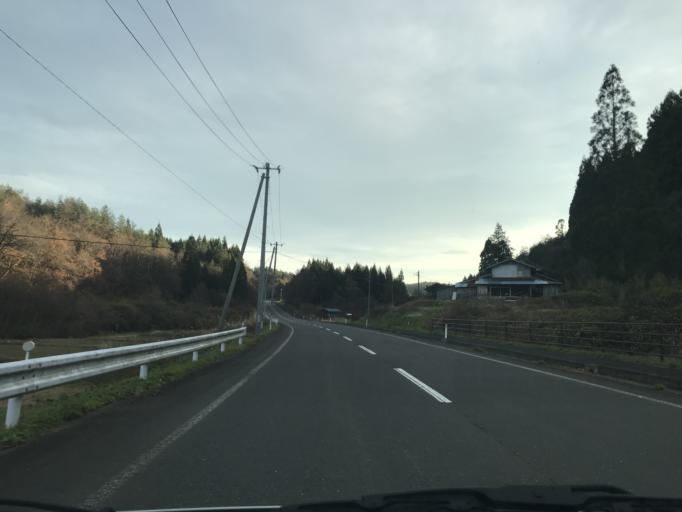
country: JP
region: Iwate
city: Ichinoseki
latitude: 38.9912
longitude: 141.0662
